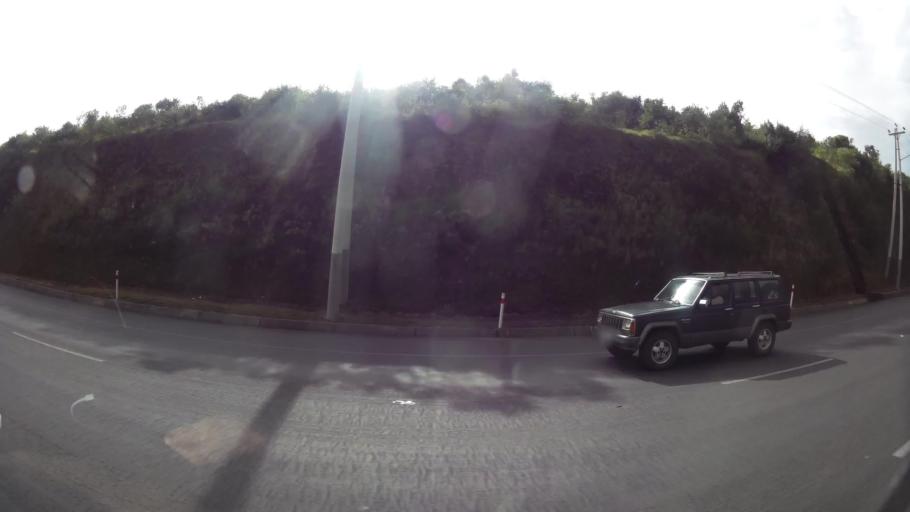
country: EC
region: Pichincha
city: Sangolqui
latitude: -0.3952
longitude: -78.5366
